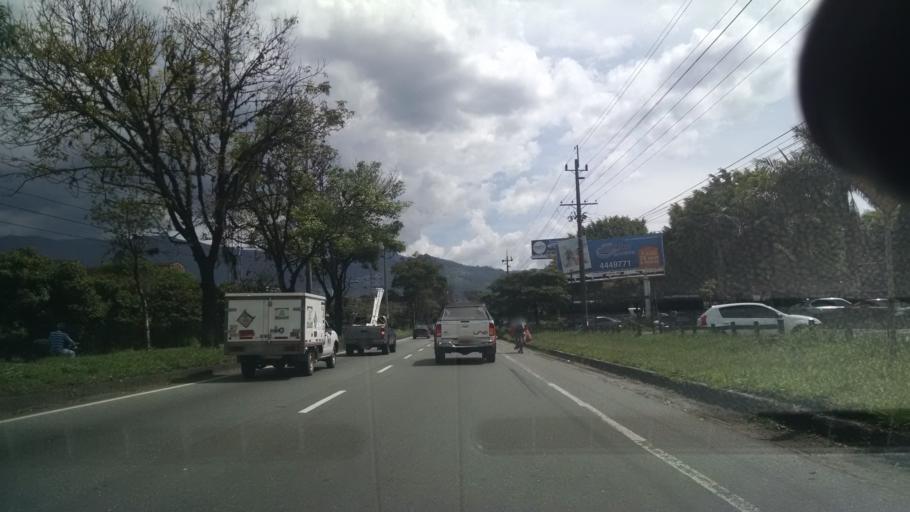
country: CO
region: Antioquia
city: Itagui
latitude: 6.1911
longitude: -75.5831
